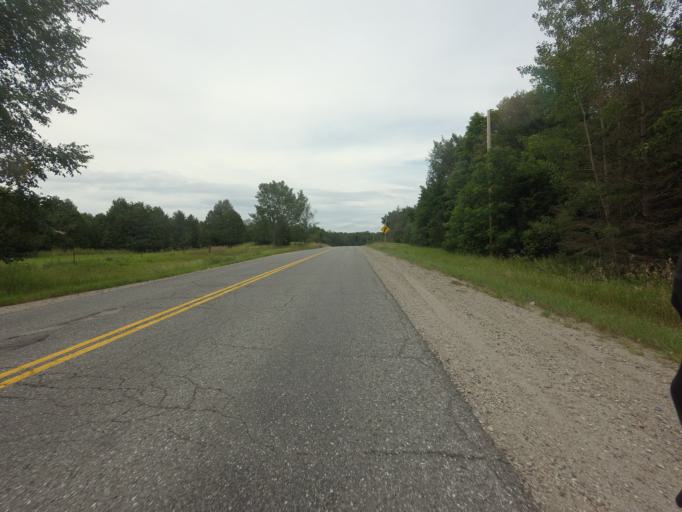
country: CA
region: Ontario
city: Carleton Place
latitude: 45.1375
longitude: -76.3283
